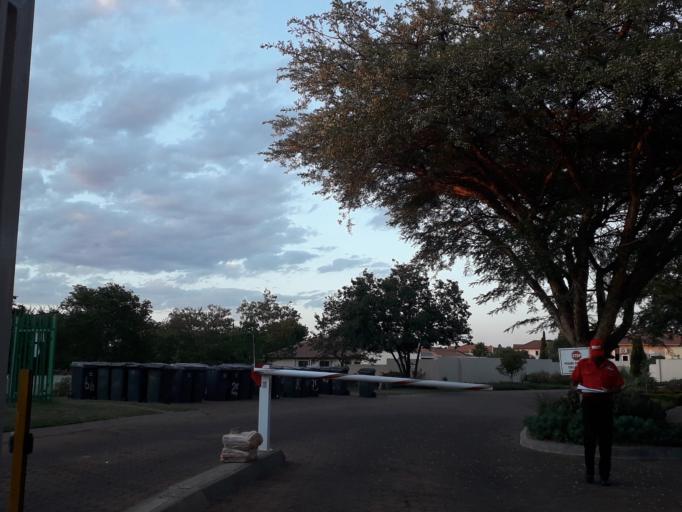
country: ZA
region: Gauteng
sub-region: City of Johannesburg Metropolitan Municipality
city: Midrand
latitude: -25.9947
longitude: 28.1027
